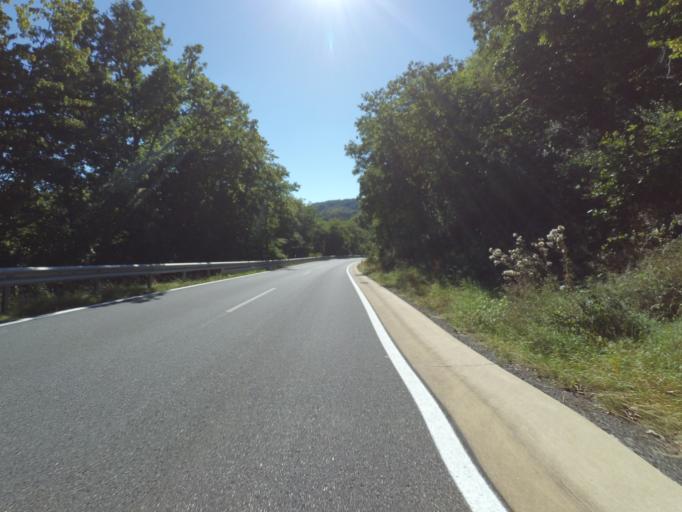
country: DE
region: Rheinland-Pfalz
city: Lutzerath
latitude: 50.1128
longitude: 6.9839
